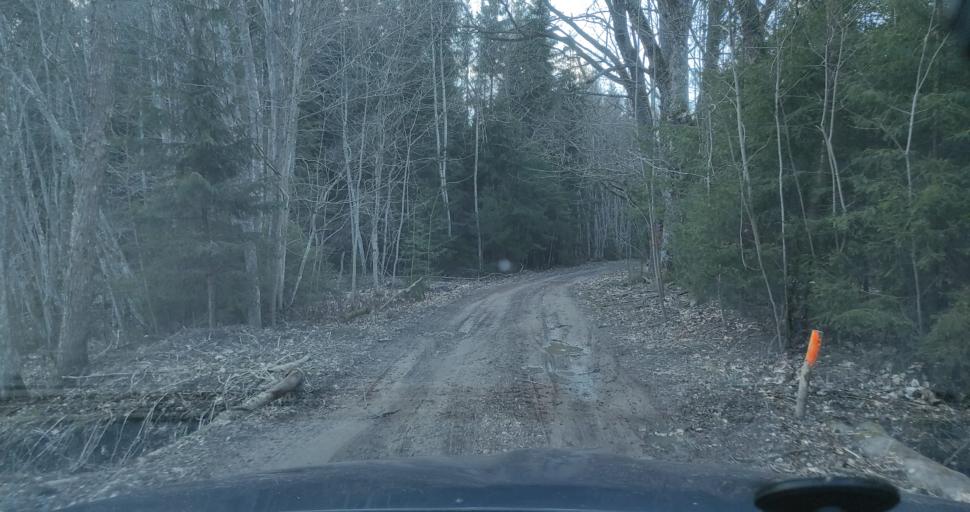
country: LV
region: Aizpute
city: Aizpute
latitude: 56.8711
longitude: 21.7545
